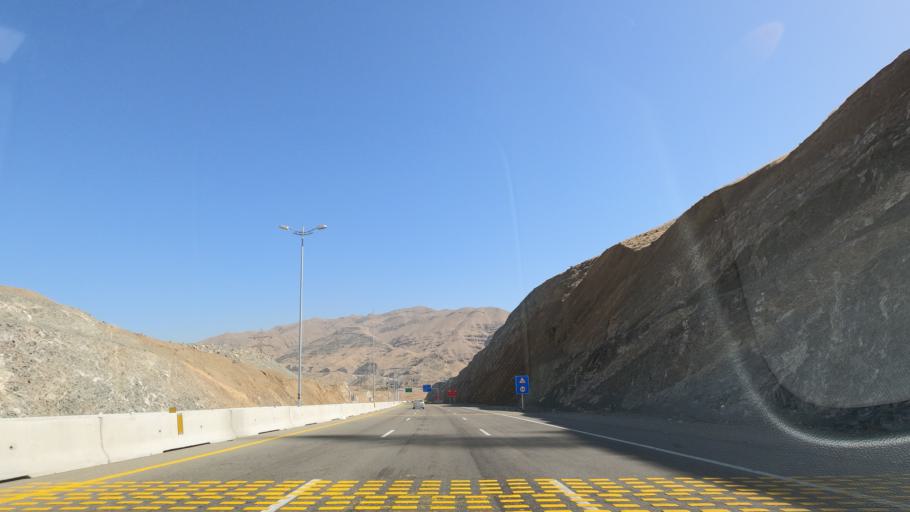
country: IR
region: Alborz
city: Karaj
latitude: 35.8170
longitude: 51.0379
